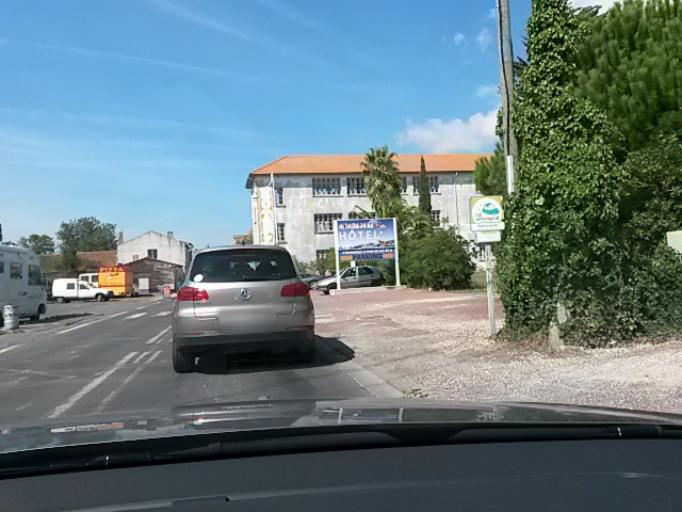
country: FR
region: Poitou-Charentes
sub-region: Departement de la Charente-Maritime
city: Saint-Denis-d'Oleron
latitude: 45.9701
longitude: -1.3495
